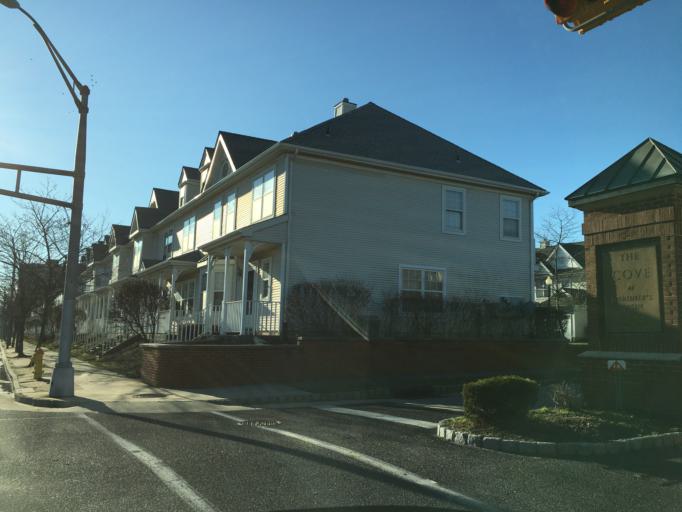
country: US
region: New Jersey
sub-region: Atlantic County
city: Atlantic City
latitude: 39.3752
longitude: -74.4178
